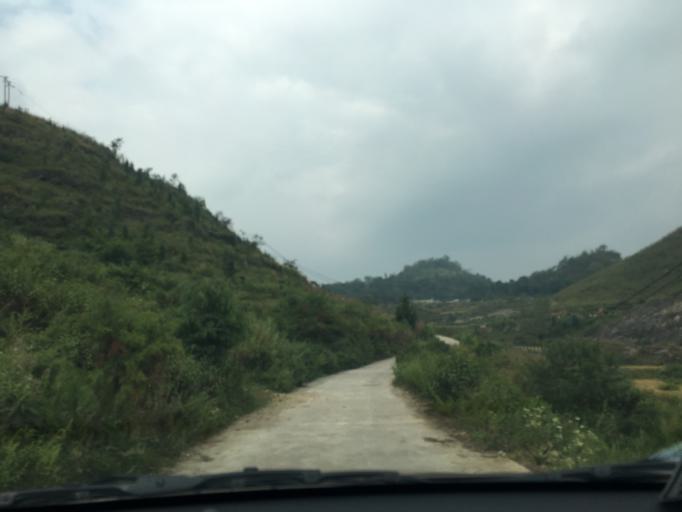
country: CN
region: Guizhou Sheng
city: Anshun
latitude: 25.5740
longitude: 105.6255
